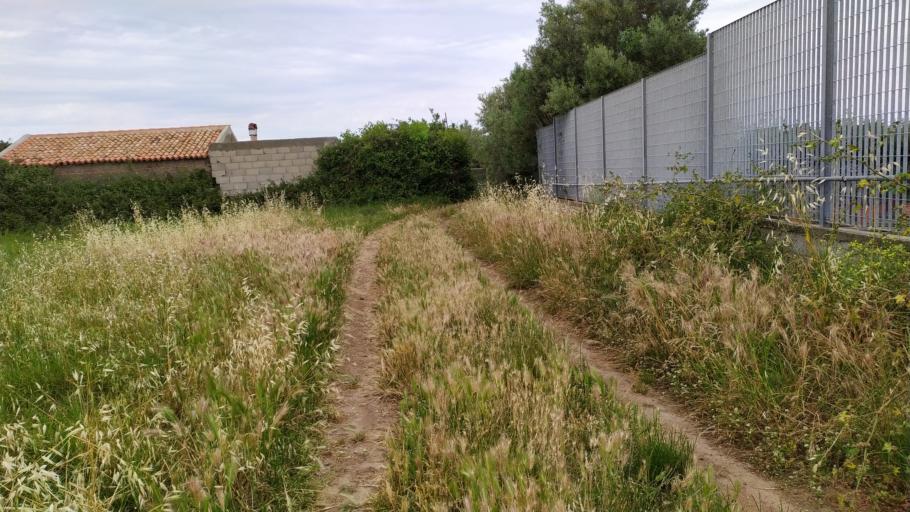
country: IT
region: Sicily
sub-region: Messina
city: San Filippo del Mela
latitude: 38.1844
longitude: 15.2640
